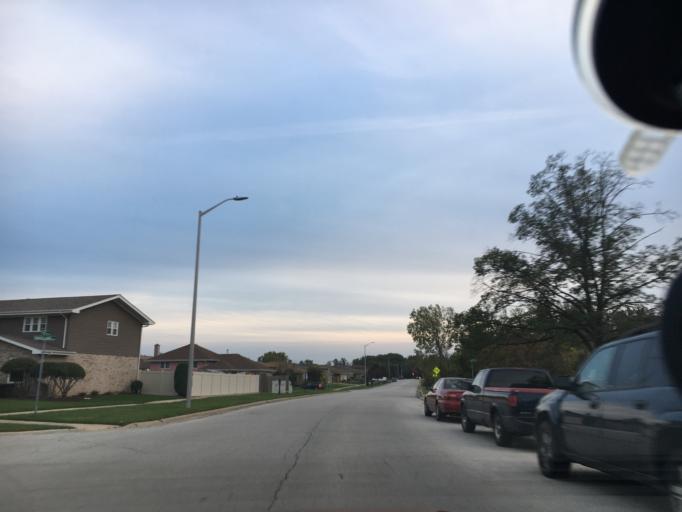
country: US
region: Illinois
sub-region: Cook County
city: Oak Forest
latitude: 41.6069
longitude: -87.7756
